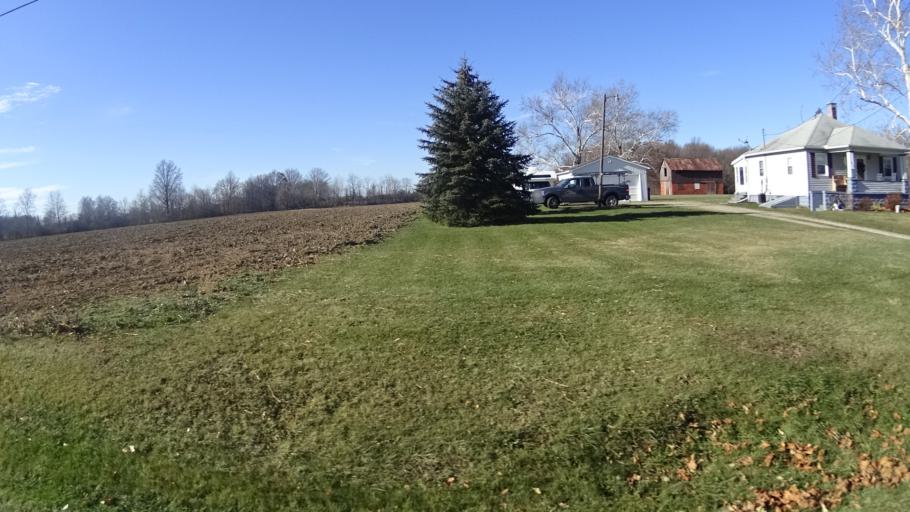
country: US
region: Ohio
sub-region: Lorain County
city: South Amherst
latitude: 41.3369
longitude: -82.2883
